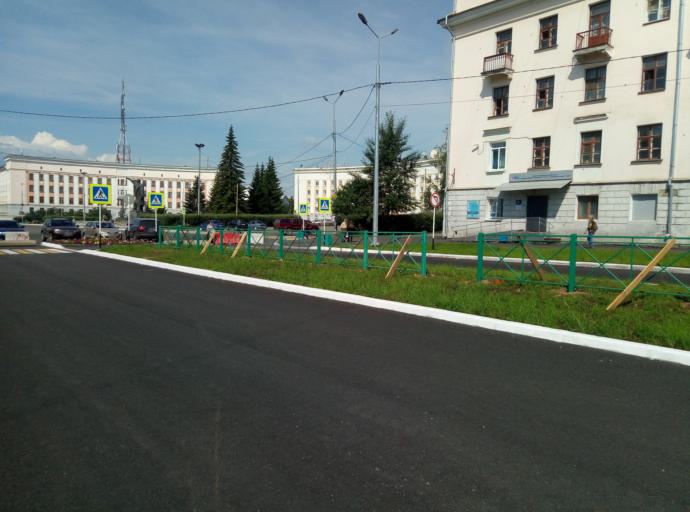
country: RU
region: Sverdlovsk
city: Krasnotur'insk
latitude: 59.7638
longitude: 60.1955
